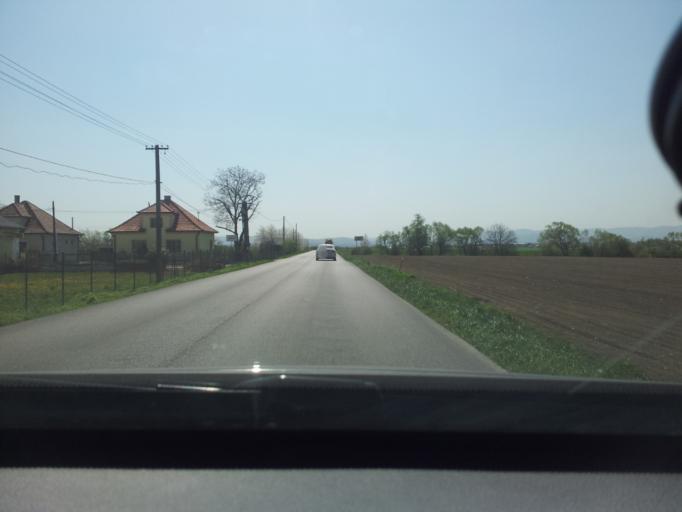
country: SK
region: Nitriansky
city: Banovce nad Bebravou
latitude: 48.6895
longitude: 18.2525
